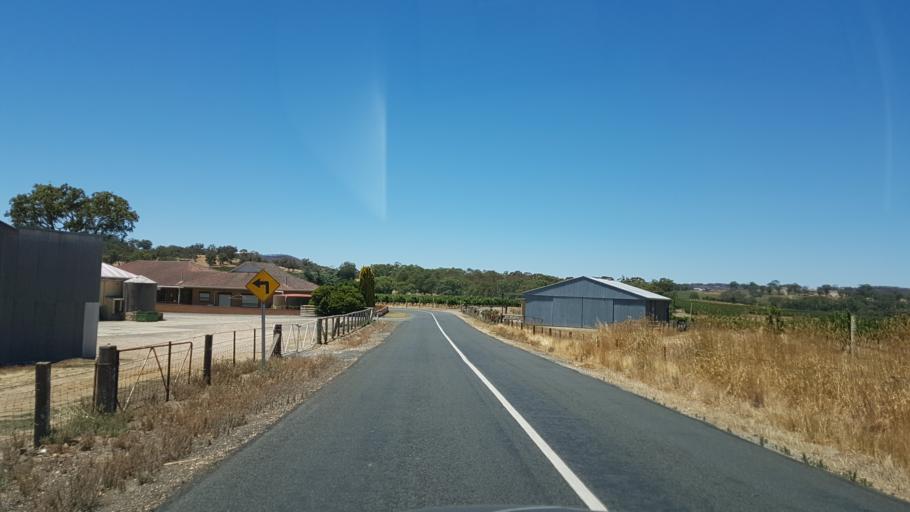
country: AU
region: South Australia
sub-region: Adelaide Hills
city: Lobethal
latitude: -34.8982
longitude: 138.9037
